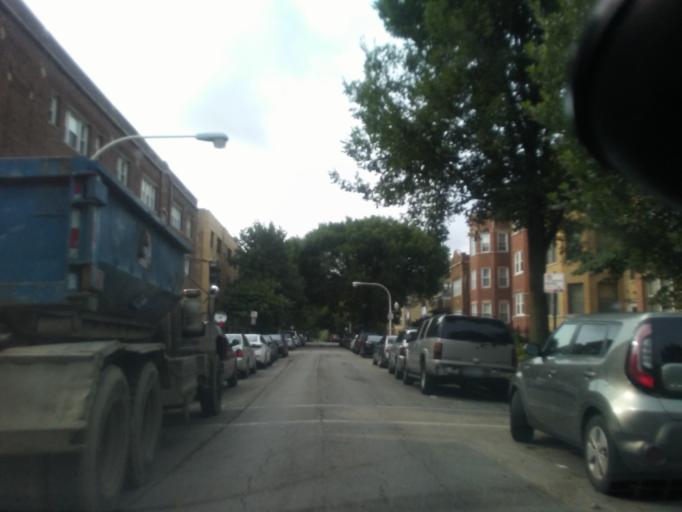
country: US
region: Illinois
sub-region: Cook County
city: Evanston
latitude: 41.9969
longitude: -87.6862
